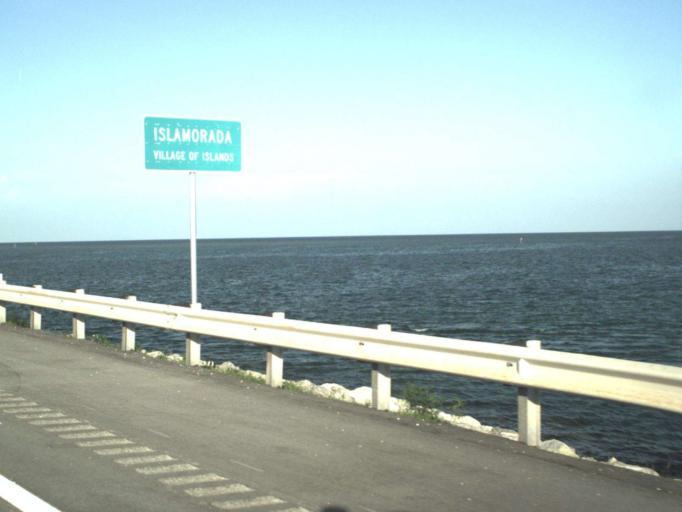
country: US
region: Florida
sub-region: Monroe County
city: Islamorada
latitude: 24.8417
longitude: -80.7529
